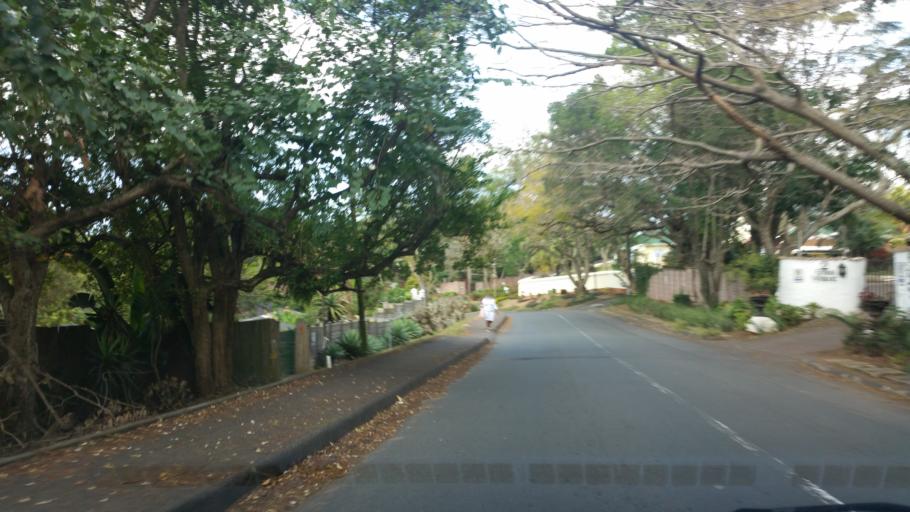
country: ZA
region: KwaZulu-Natal
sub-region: eThekwini Metropolitan Municipality
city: Berea
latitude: -29.8320
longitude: 30.8984
